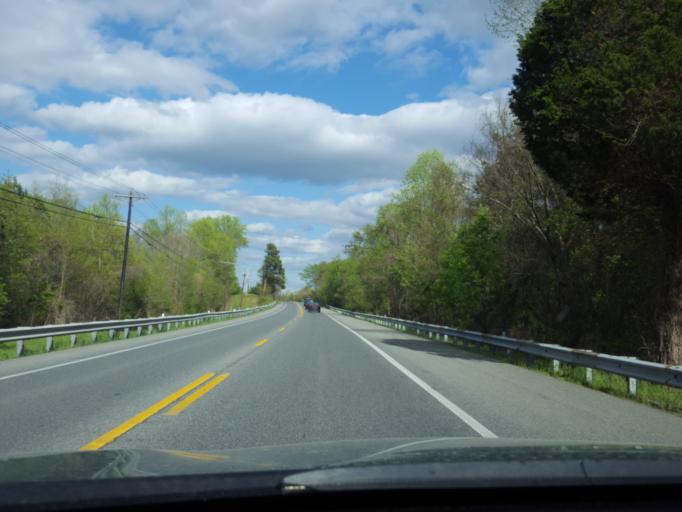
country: US
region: Maryland
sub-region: Saint Mary's County
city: Golden Beach
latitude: 38.5146
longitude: -76.7017
